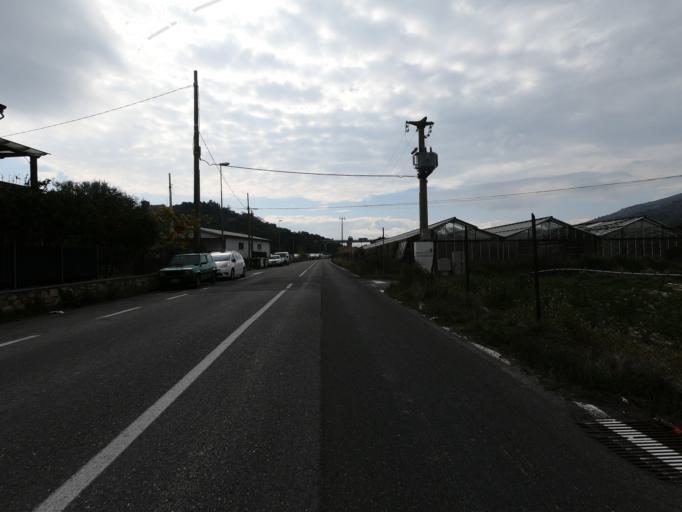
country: IT
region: Liguria
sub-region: Provincia di Savona
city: Andora
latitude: 43.9699
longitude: 8.1401
